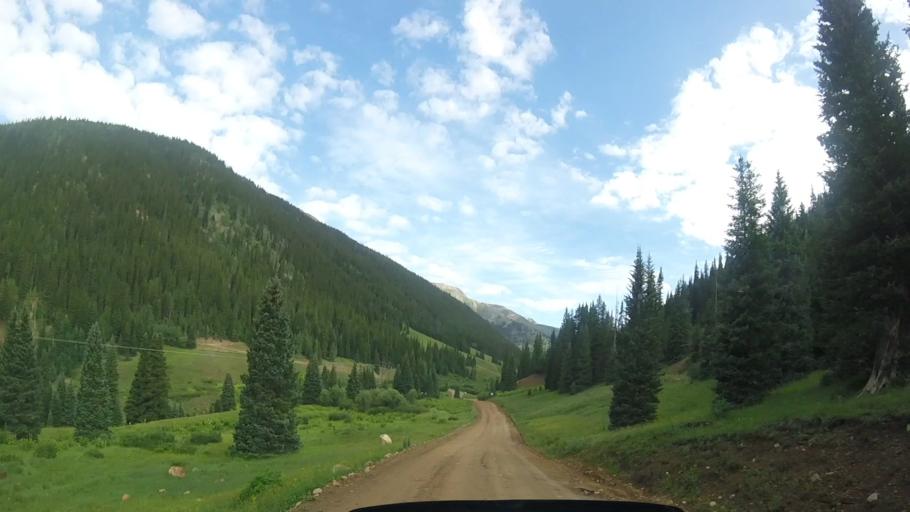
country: US
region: Colorado
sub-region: San Juan County
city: Silverton
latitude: 37.8485
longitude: -107.7254
